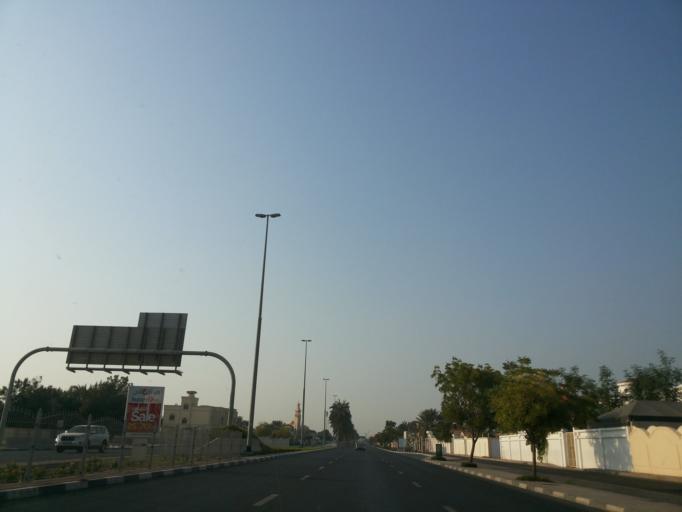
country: AE
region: Ash Shariqah
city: Sharjah
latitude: 25.2915
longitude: 55.3441
